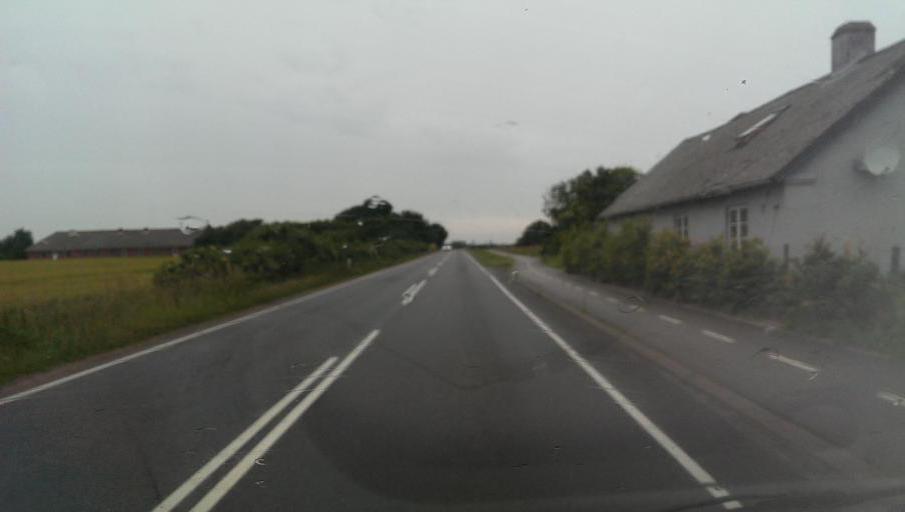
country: DK
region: South Denmark
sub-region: Varde Kommune
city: Oksbol
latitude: 55.7019
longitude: 8.3588
